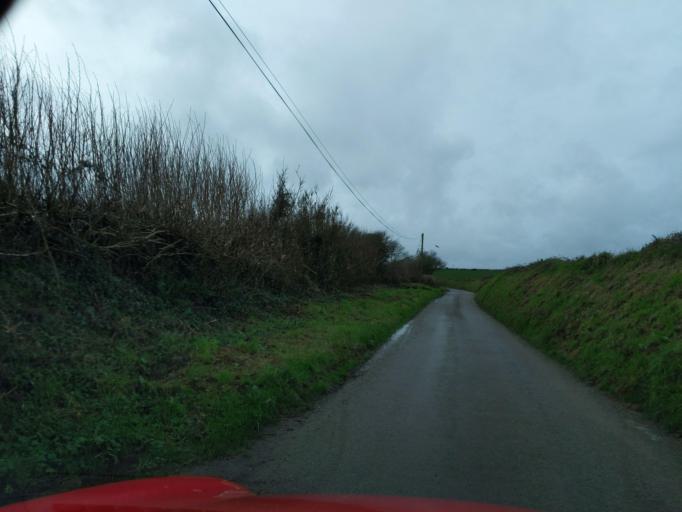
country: GB
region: England
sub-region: Cornwall
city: Duloe
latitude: 50.3496
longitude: -4.5484
